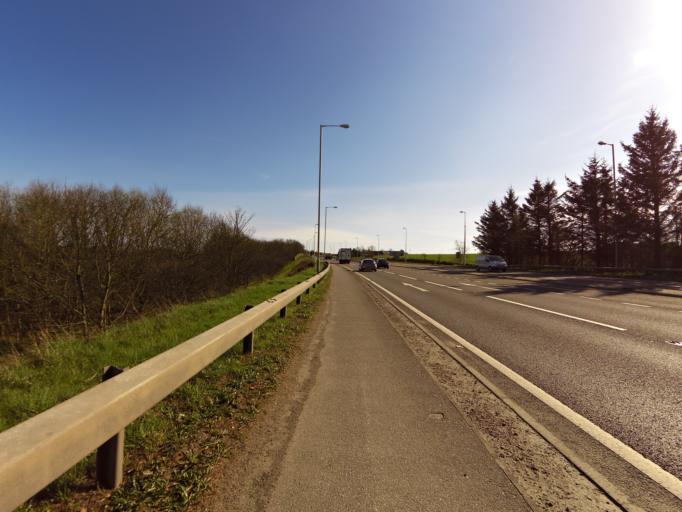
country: GB
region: Scotland
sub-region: Aberdeenshire
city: Newtonhill
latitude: 57.0402
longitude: -2.1536
